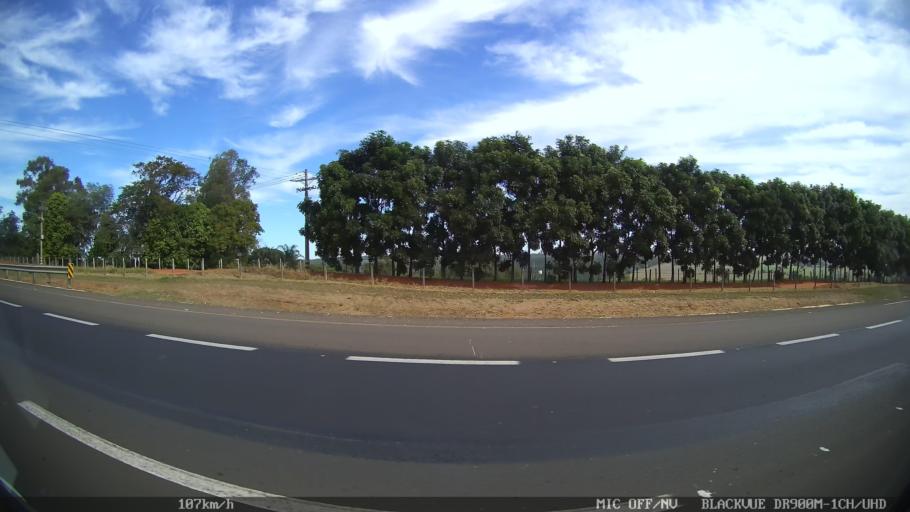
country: BR
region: Sao Paulo
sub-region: Matao
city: Matao
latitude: -21.5958
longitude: -48.4379
